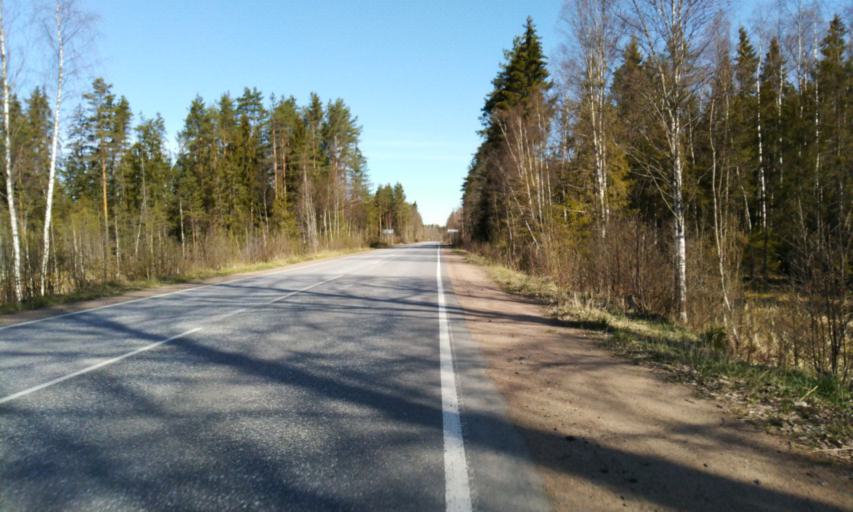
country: RU
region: Leningrad
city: Garbolovo
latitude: 60.3332
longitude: 30.4411
